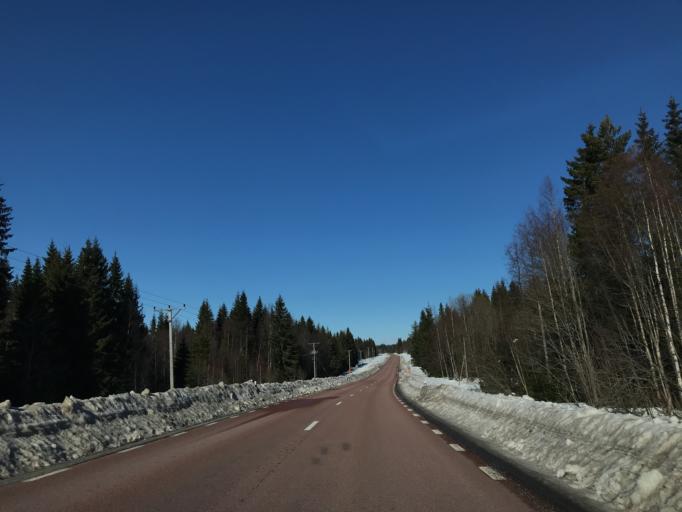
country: SE
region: Dalarna
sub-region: Vansbro Kommun
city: Vansbro
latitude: 60.3298
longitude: 14.2001
